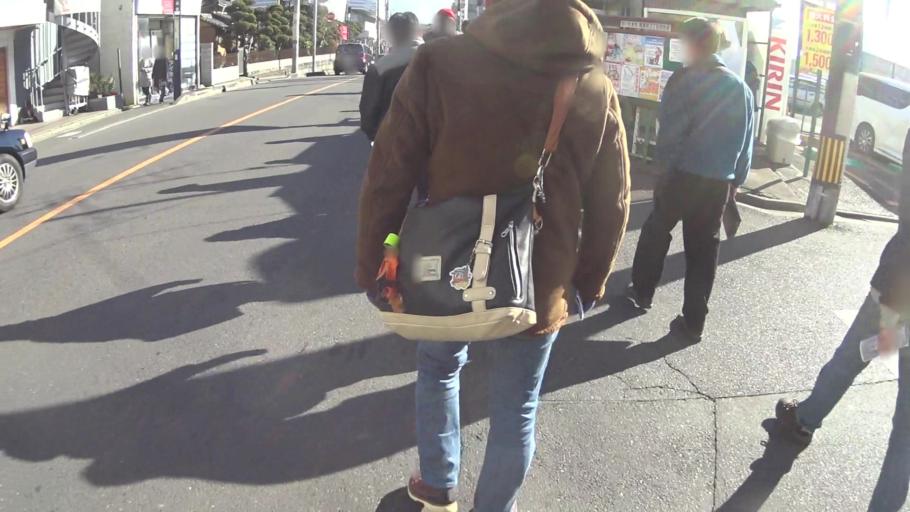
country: JP
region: Saitama
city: Shimotoda
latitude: 35.8470
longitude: 139.6705
